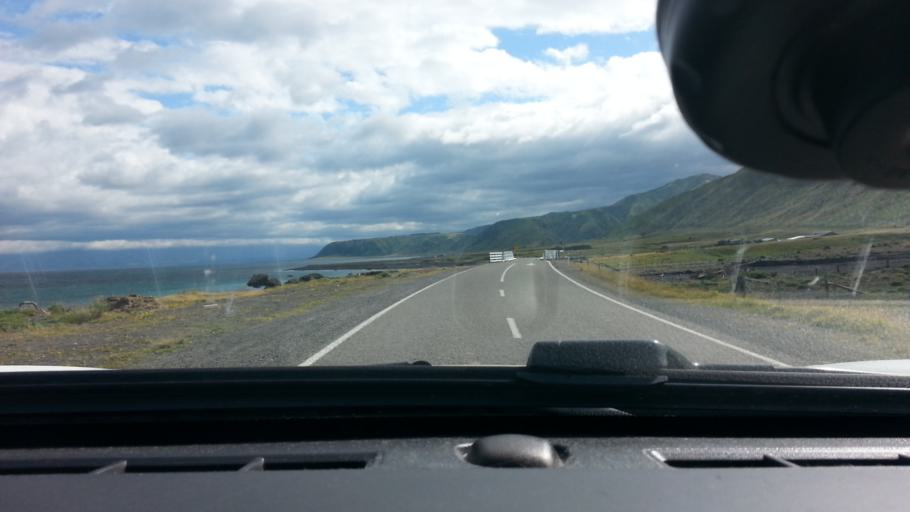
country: NZ
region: Wellington
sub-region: South Wairarapa District
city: Waipawa
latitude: -41.5780
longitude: 175.2258
